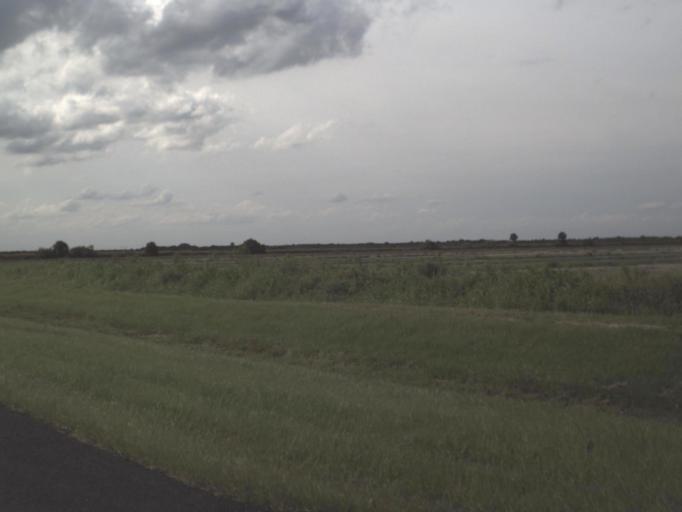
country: US
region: Florida
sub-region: Glades County
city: Moore Haven
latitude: 26.7533
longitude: -81.1104
